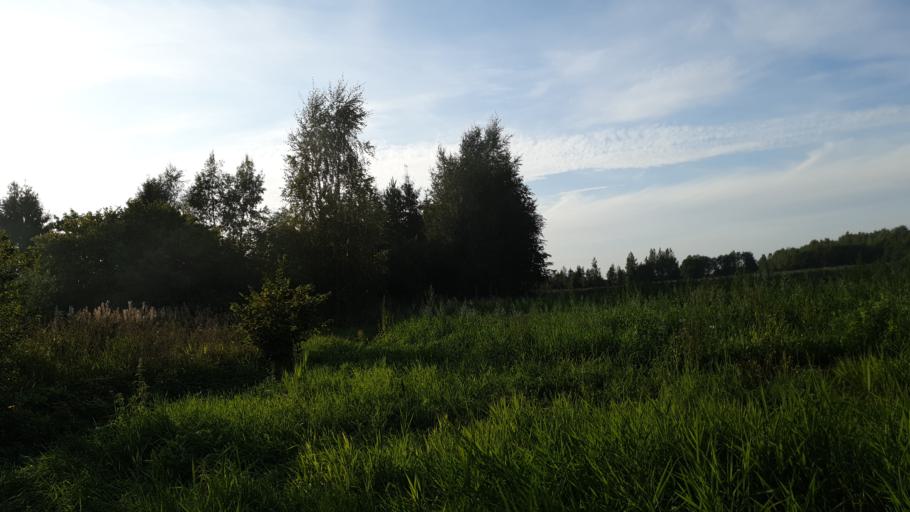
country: RU
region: Leningrad
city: Ivangorod
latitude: 59.4276
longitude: 28.3261
